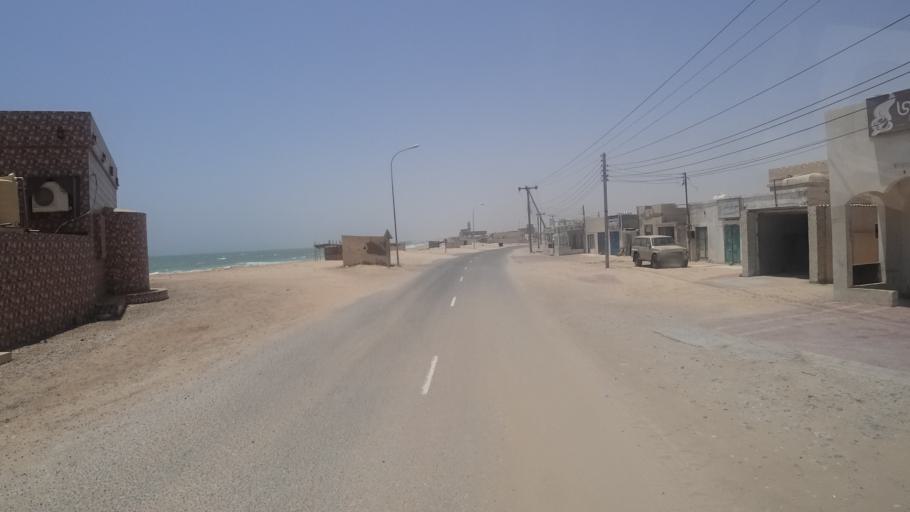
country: OM
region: Ash Sharqiyah
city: Sur
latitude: 22.0858
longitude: 59.6878
